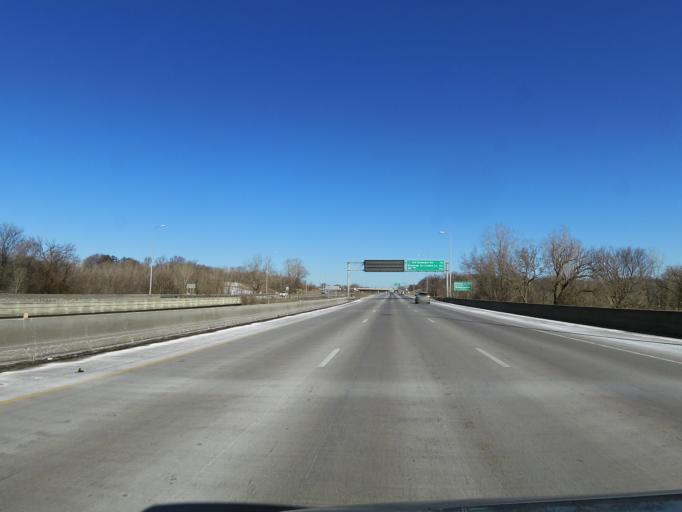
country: US
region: Minnesota
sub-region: Hennepin County
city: Bloomington
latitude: 44.8347
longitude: -93.2391
